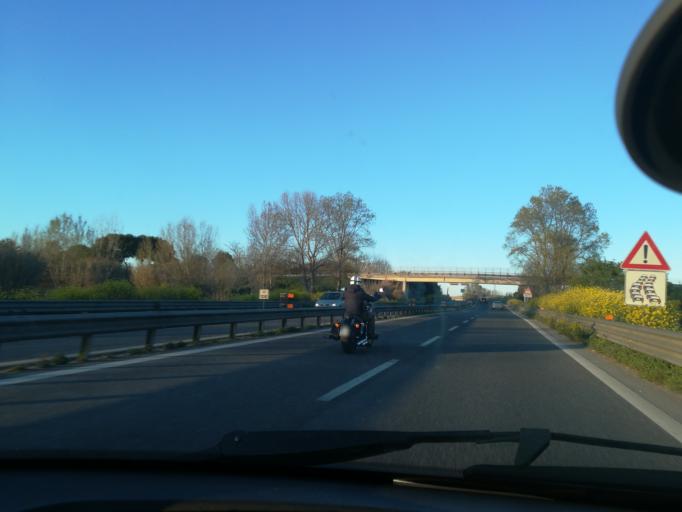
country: IT
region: The Marches
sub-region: Provincia di Macerata
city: Santa Maria Apparente
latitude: 43.2892
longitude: 13.7107
